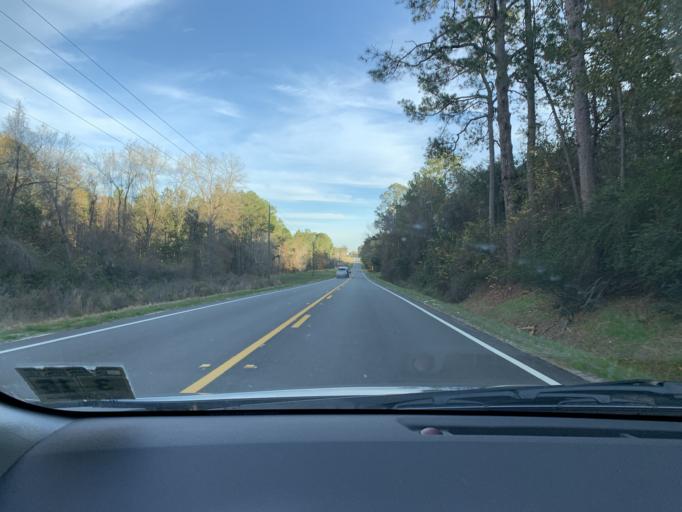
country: US
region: Georgia
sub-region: Coffee County
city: Broxton
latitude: 31.5818
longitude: -83.0659
